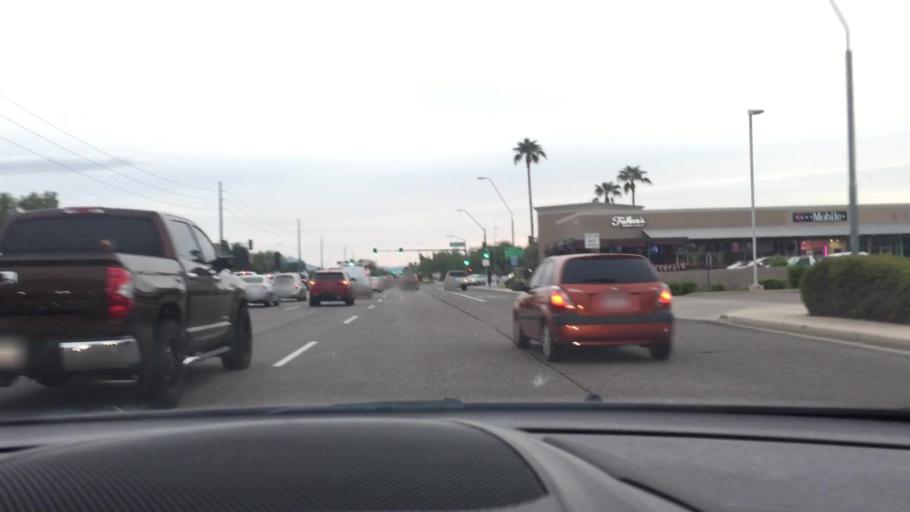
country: US
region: Arizona
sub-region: Maricopa County
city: Guadalupe
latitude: 33.3054
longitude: -111.9790
